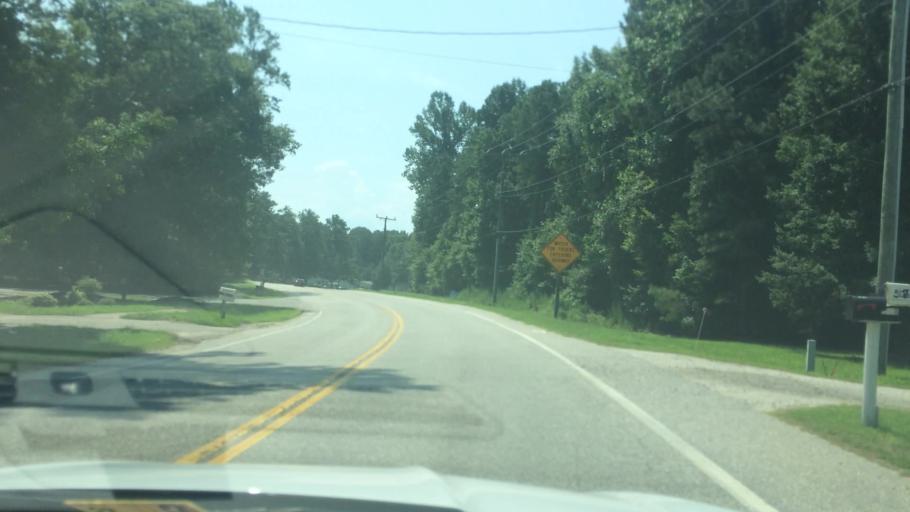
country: US
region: Virginia
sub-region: James City County
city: Williamsburg
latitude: 37.3228
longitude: -76.7895
